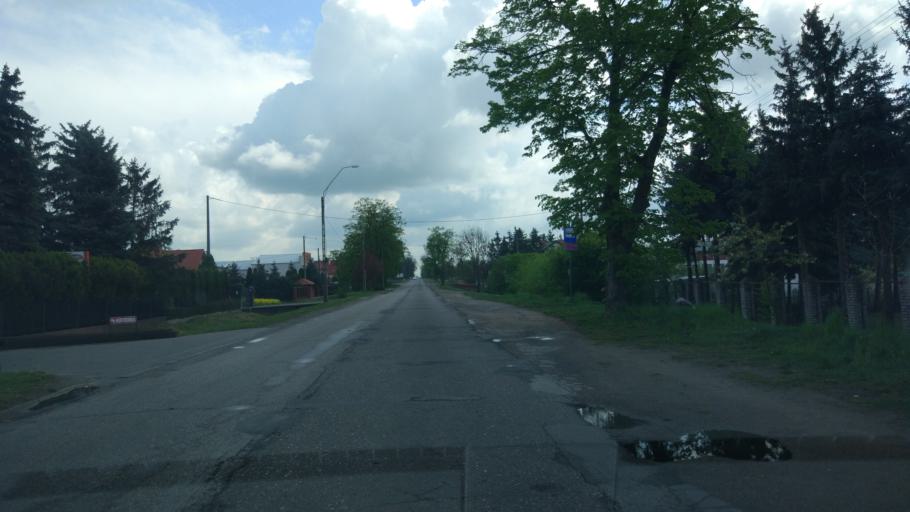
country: PL
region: Lodz Voivodeship
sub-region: Powiat kutnowski
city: Kutno
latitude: 52.2268
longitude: 19.3921
